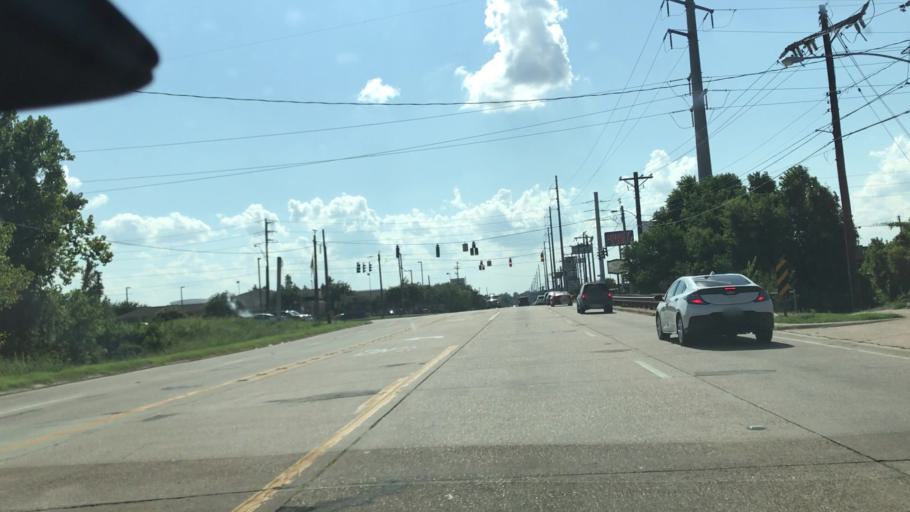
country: US
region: Louisiana
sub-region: Bossier Parish
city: Bossier City
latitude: 32.4434
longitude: -93.7124
